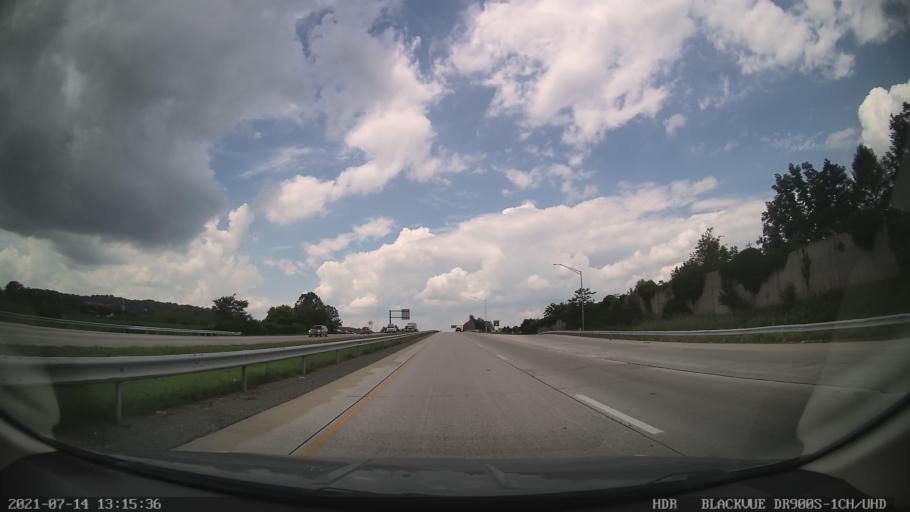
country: US
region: Pennsylvania
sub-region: Berks County
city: Spring Ridge
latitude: 40.3565
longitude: -75.9751
